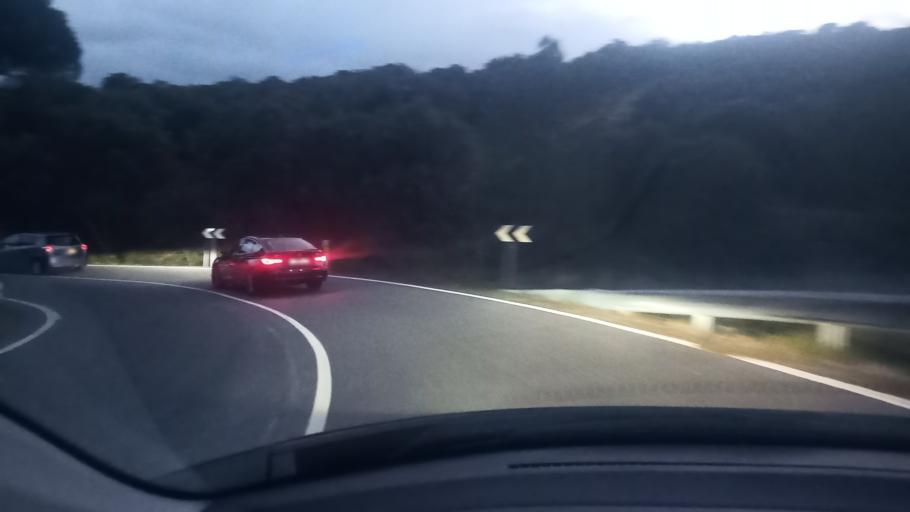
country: ES
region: Madrid
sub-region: Provincia de Madrid
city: Navas del Rey
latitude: 40.4401
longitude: -4.2665
